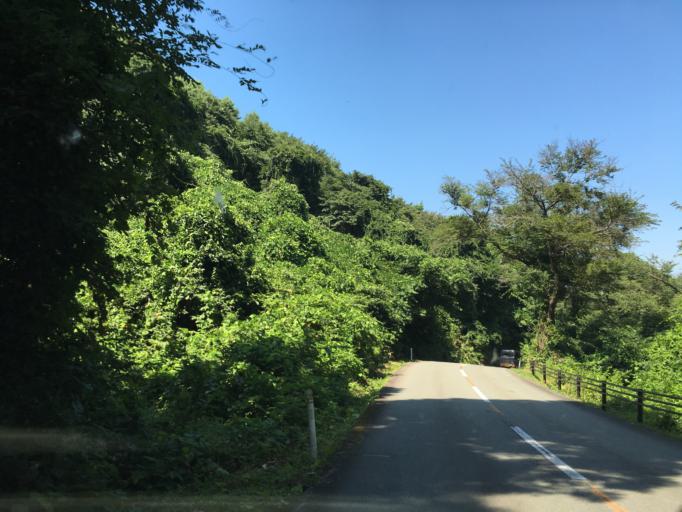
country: JP
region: Akita
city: Tenno
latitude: 39.9290
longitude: 139.8801
